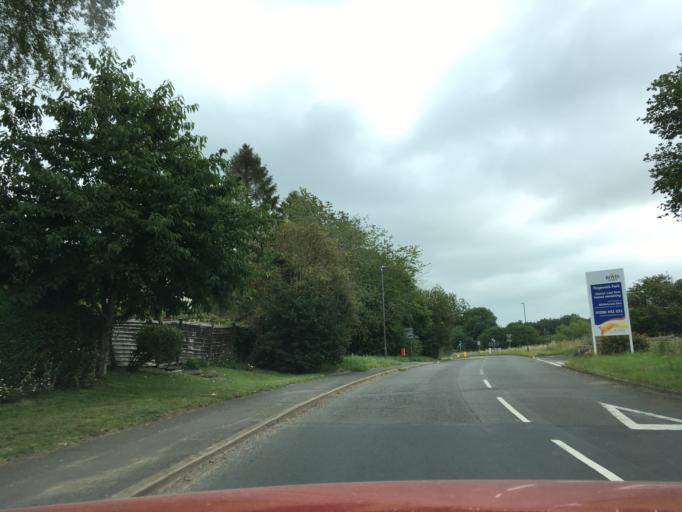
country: GB
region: England
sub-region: Buckinghamshire
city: Buckingham
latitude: 51.9908
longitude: -1.0414
